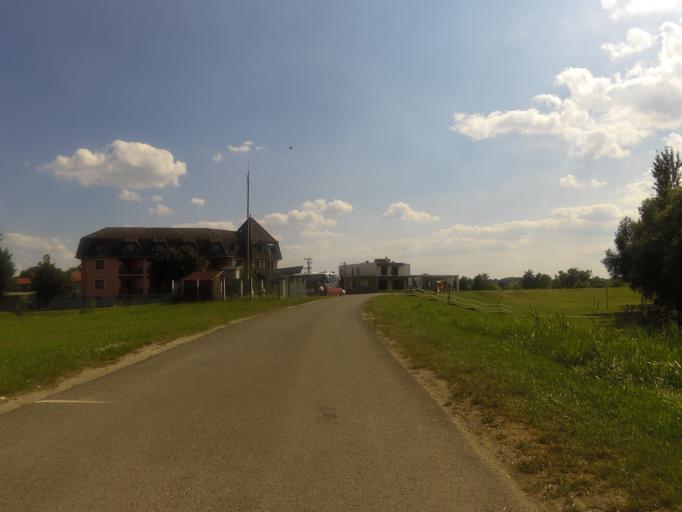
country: HU
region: Jasz-Nagykun-Szolnok
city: Tiszafured
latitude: 47.6068
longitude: 20.7179
